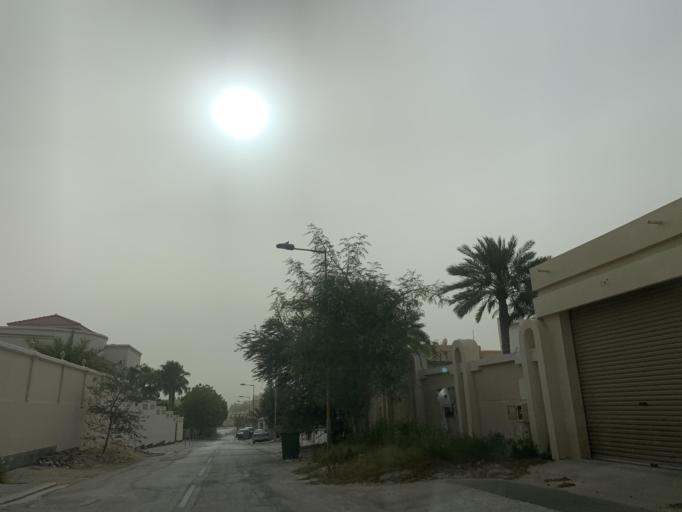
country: BH
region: Northern
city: Ar Rifa'
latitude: 26.1422
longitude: 50.5318
